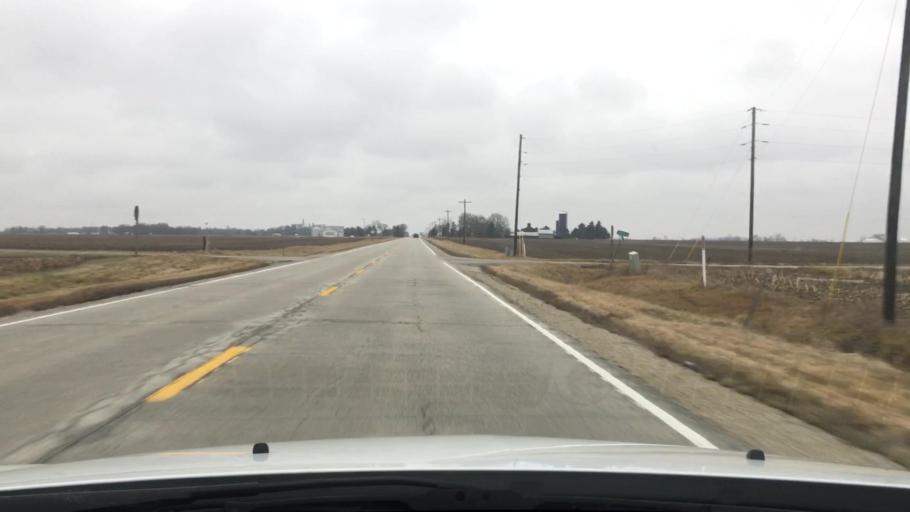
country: US
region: Illinois
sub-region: Iroquois County
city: Clifton
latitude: 40.8856
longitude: -87.9228
